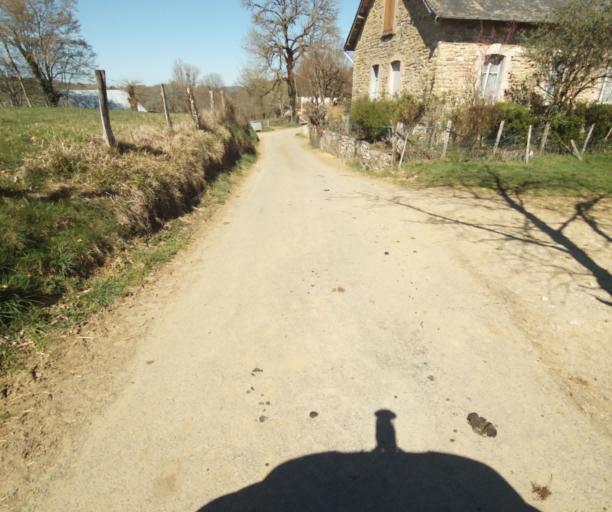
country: FR
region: Limousin
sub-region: Departement de la Correze
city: Chamboulive
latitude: 45.4501
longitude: 1.6649
